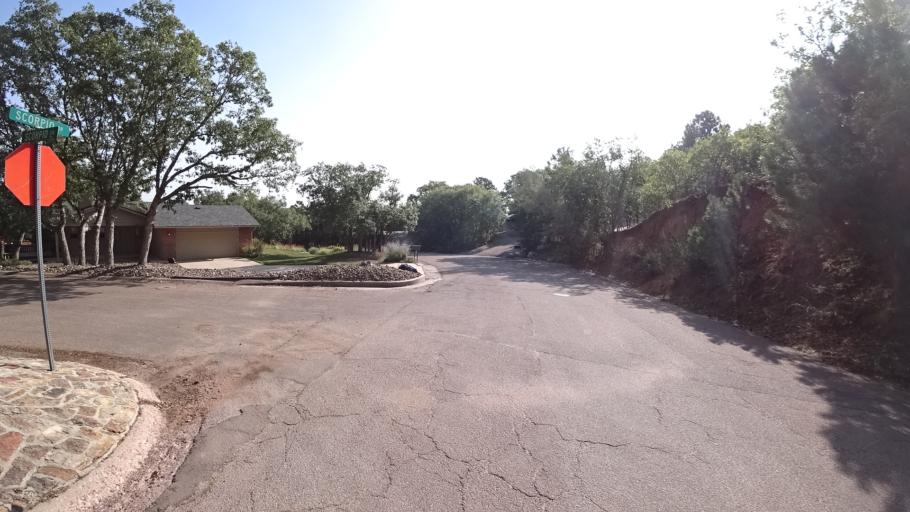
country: US
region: Colorado
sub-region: El Paso County
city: Colorado Springs
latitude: 38.8142
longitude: -104.8657
